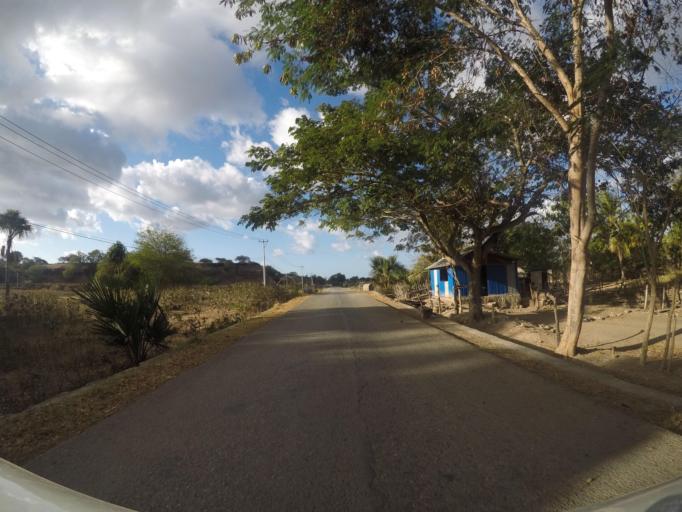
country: TL
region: Lautem
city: Lospalos
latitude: -8.4046
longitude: 126.8300
